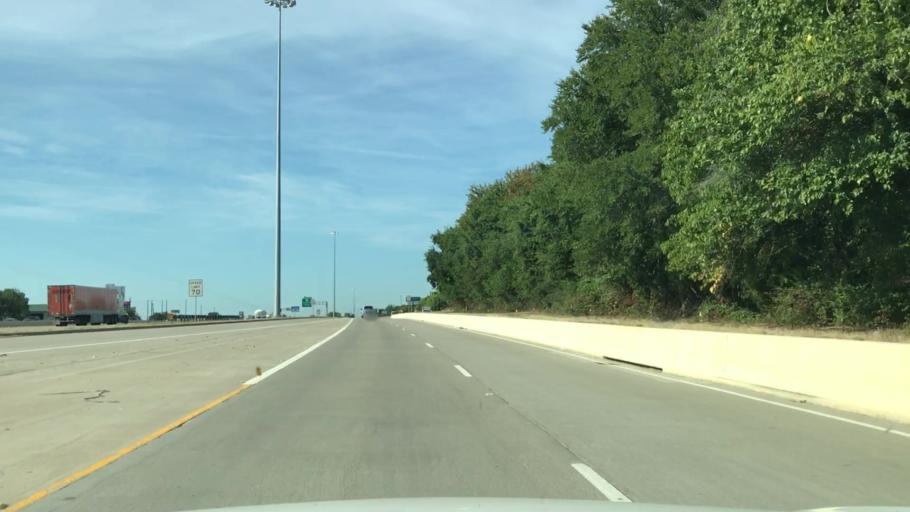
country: US
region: Texas
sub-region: Collin County
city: McKinney
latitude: 33.2375
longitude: -96.6313
